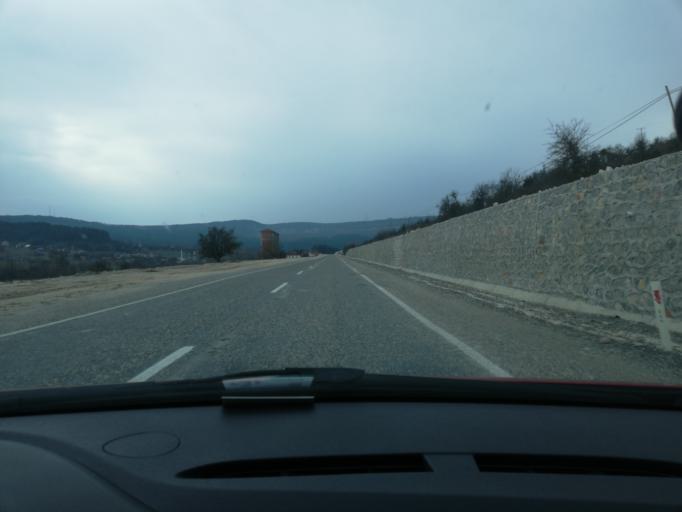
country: TR
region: Kastamonu
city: Pinarbasi
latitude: 41.5949
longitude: 33.0991
